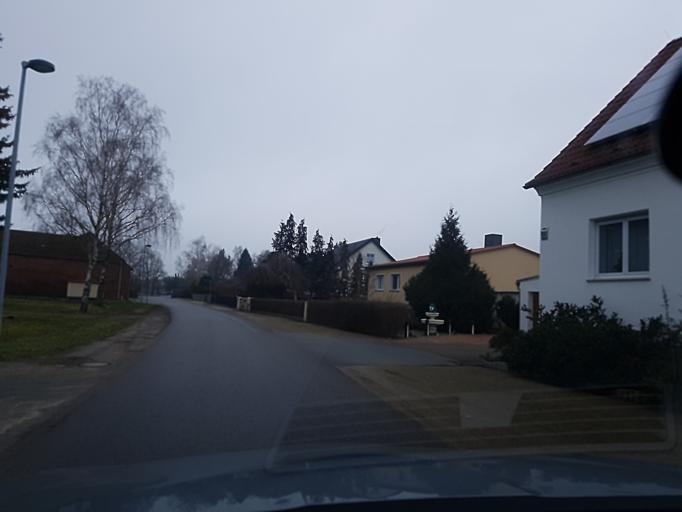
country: DE
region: Brandenburg
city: Schonewalde
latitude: 51.6573
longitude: 13.5995
